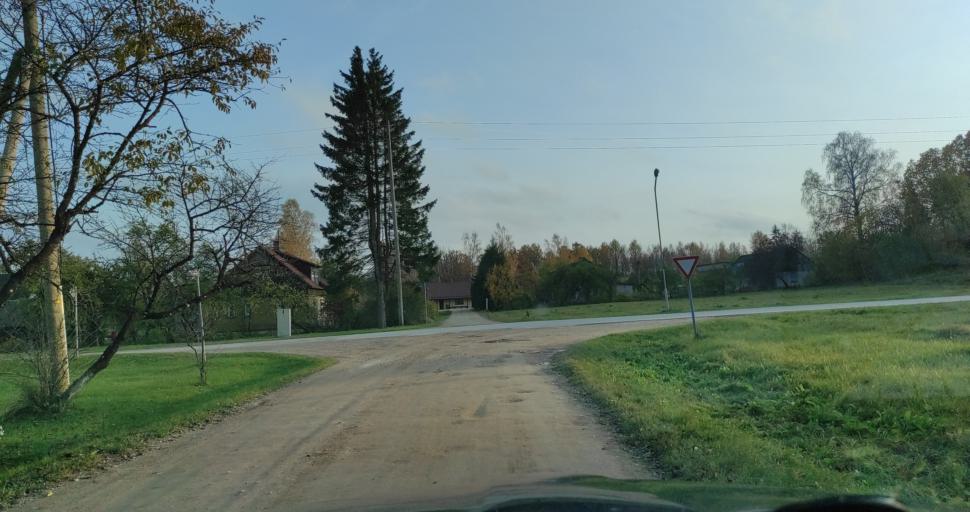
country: LV
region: Vainode
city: Vainode
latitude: 56.4228
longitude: 21.8750
